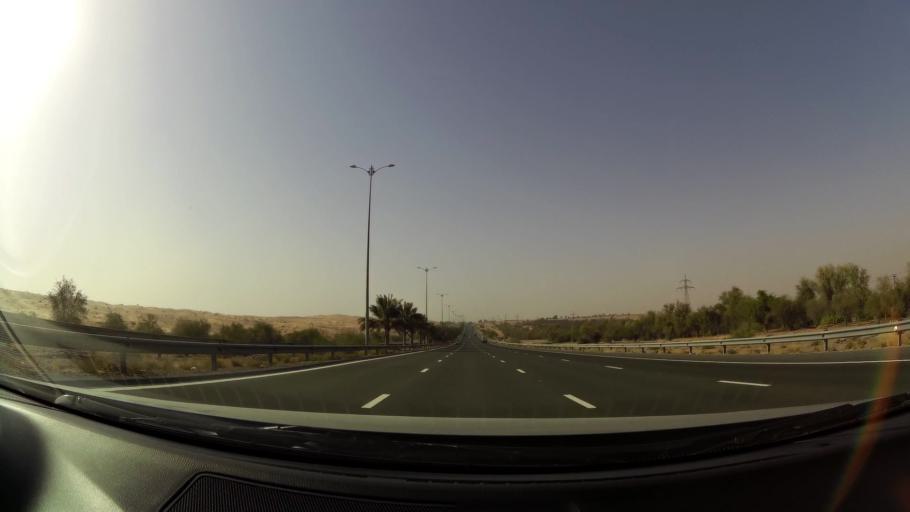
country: OM
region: Al Buraimi
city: Al Buraymi
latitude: 24.6277
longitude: 55.7222
